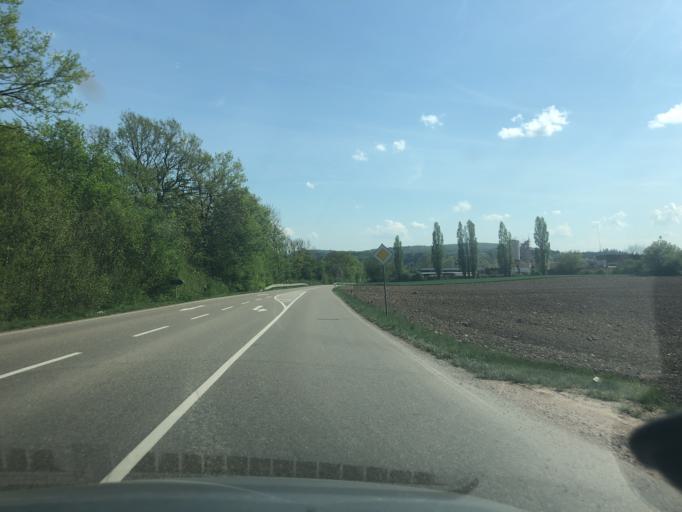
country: CH
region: Aargau
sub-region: Bezirk Zurzach
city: Koblenz
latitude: 47.6274
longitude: 8.2555
